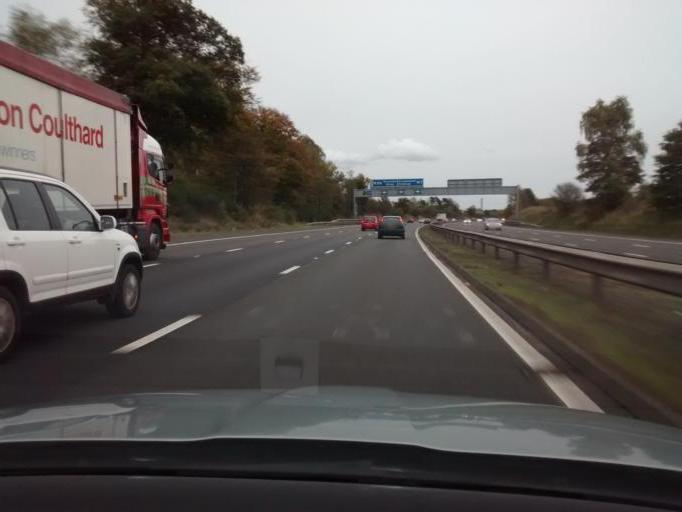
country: GB
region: Scotland
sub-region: Falkirk
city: Larbert
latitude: 56.0450
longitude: -3.8007
